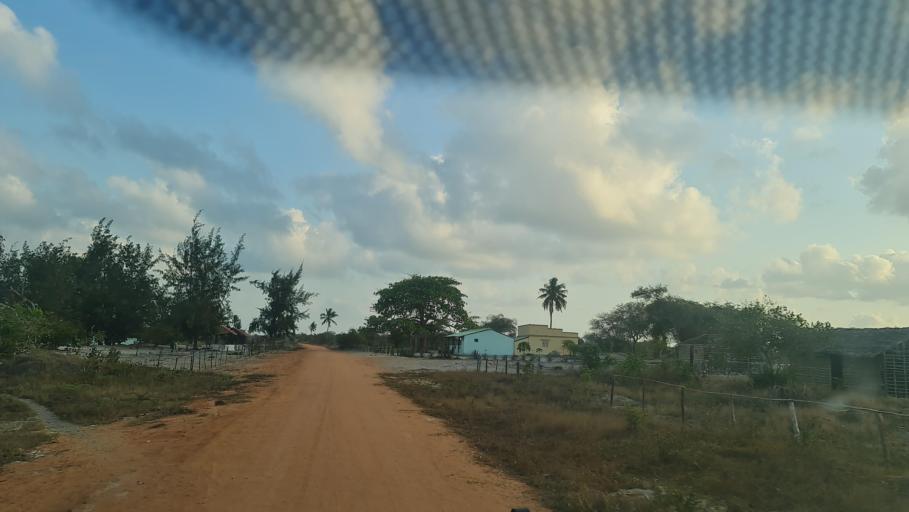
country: MZ
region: Nampula
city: Nacala
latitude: -14.7836
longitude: 40.8208
